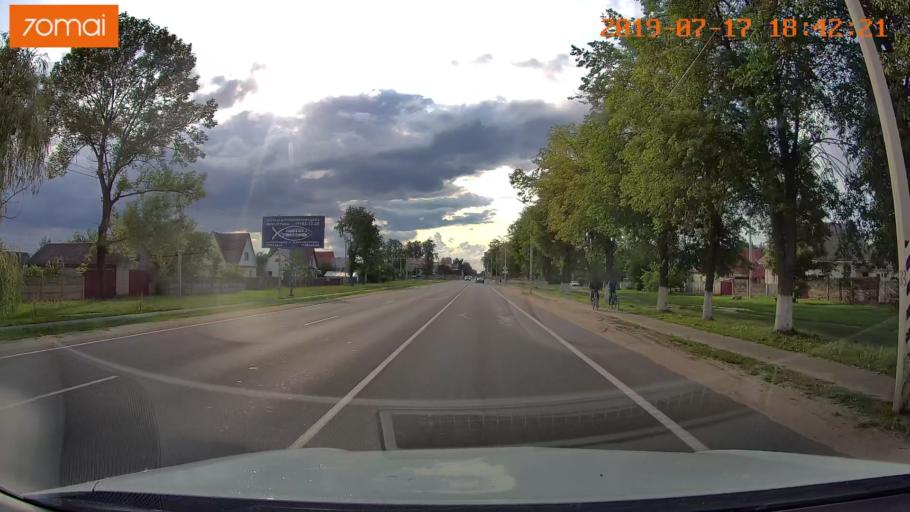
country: BY
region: Mogilev
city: Asipovichy
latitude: 53.3094
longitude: 28.6505
